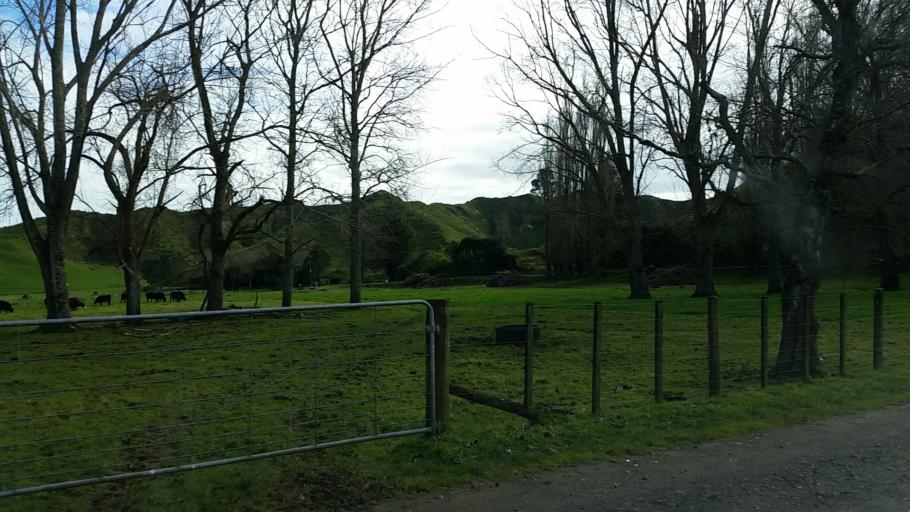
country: NZ
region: Taranaki
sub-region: South Taranaki District
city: Eltham
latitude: -39.2517
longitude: 174.5423
